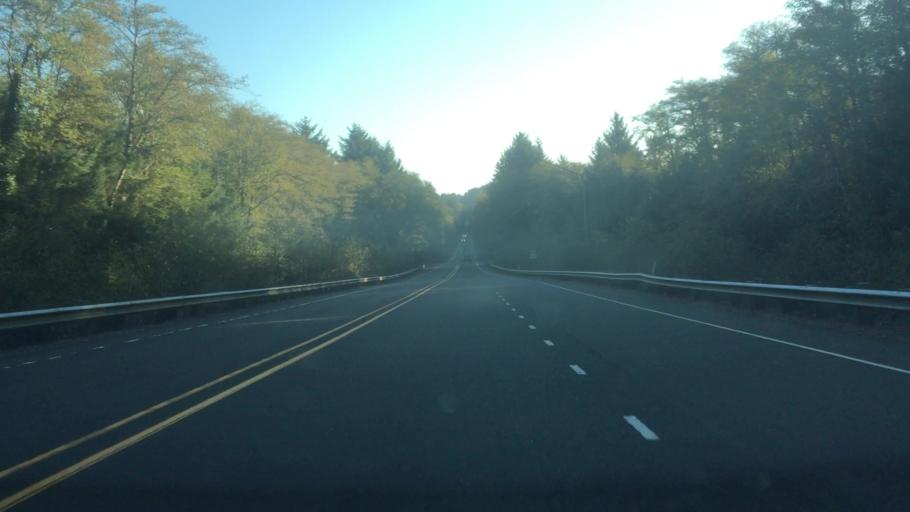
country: US
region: Oregon
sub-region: Clatsop County
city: Cannon Beach
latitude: 45.9009
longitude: -123.9534
